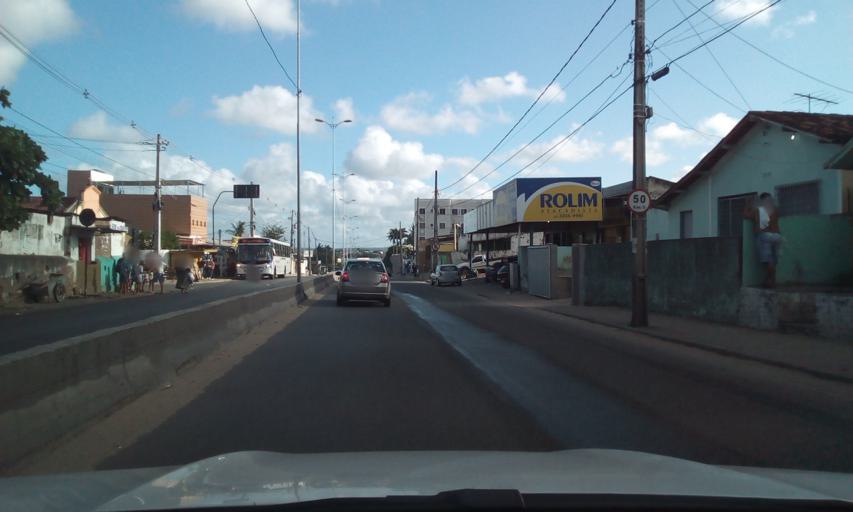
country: BR
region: Paraiba
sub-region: Bayeux
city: Bayeux
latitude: -7.1604
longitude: -34.8963
